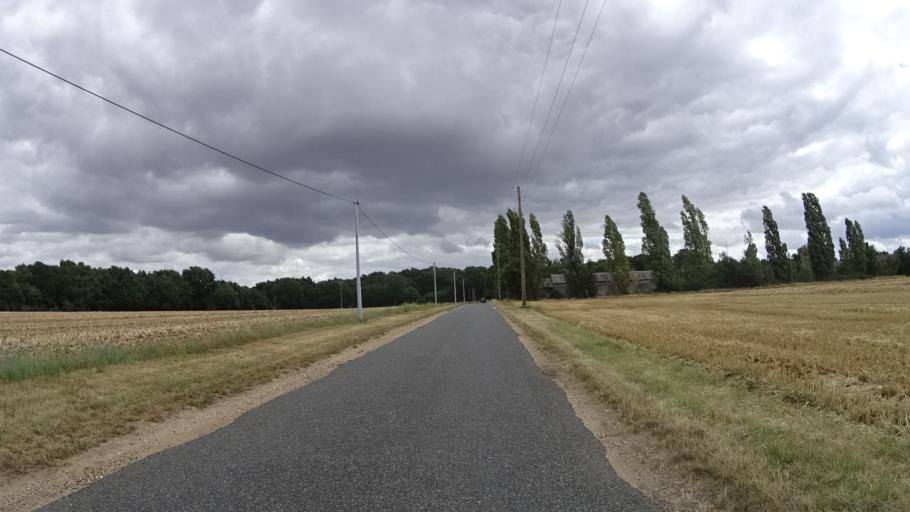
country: FR
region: Centre
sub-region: Departement du Loiret
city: Amilly
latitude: 47.9482
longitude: 2.8010
